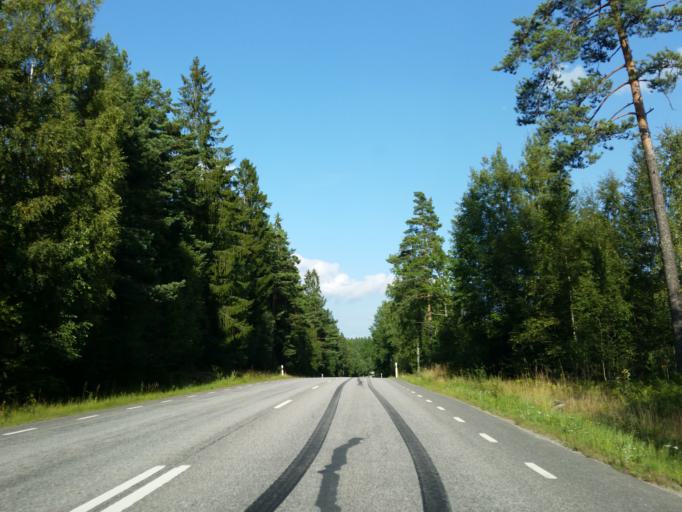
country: SE
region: Stockholm
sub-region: Nykvarns Kommun
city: Nykvarn
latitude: 59.2085
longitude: 17.3431
